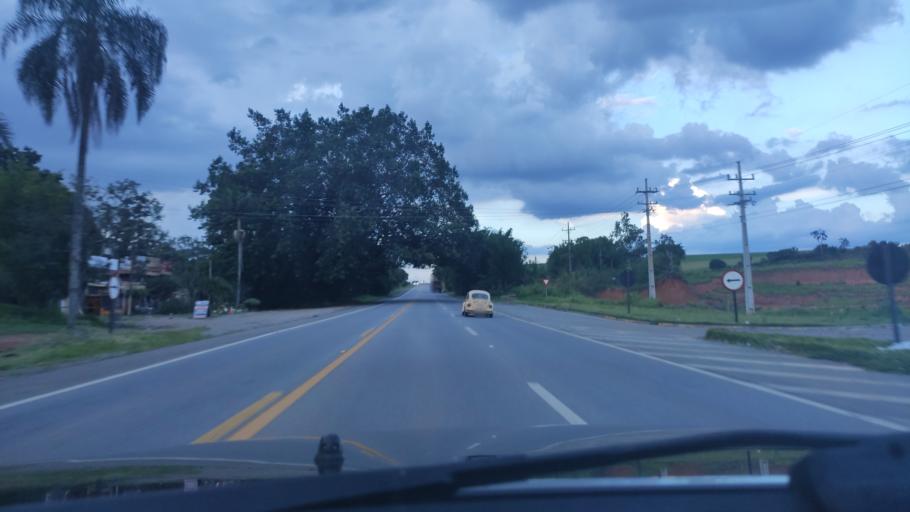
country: BR
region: Sao Paulo
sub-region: Braganca Paulista
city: Braganca Paulista
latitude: -22.8908
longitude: -46.5413
